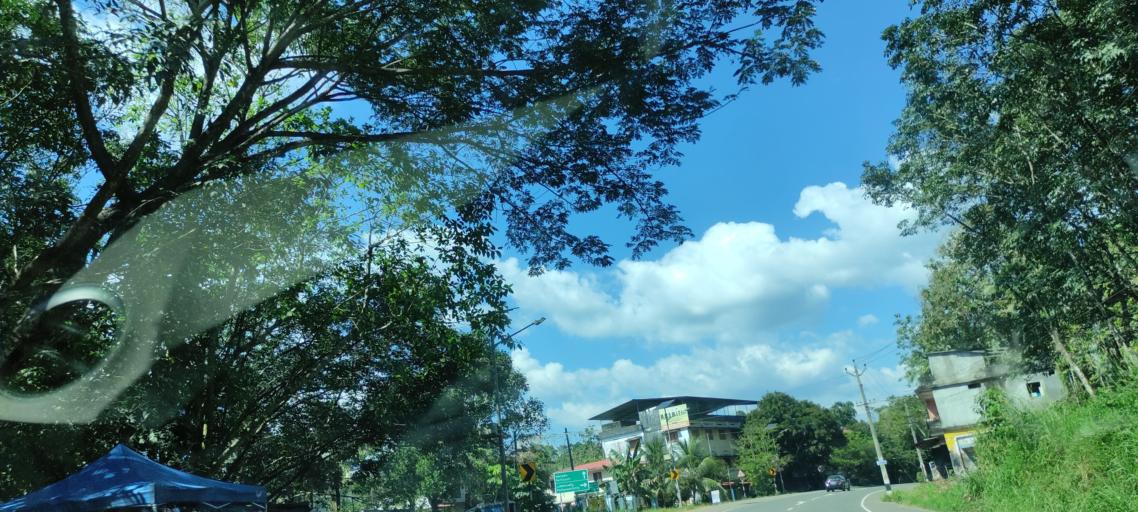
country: IN
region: Kerala
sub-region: Pattanamtitta
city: Adur
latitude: 9.1386
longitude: 76.7344
